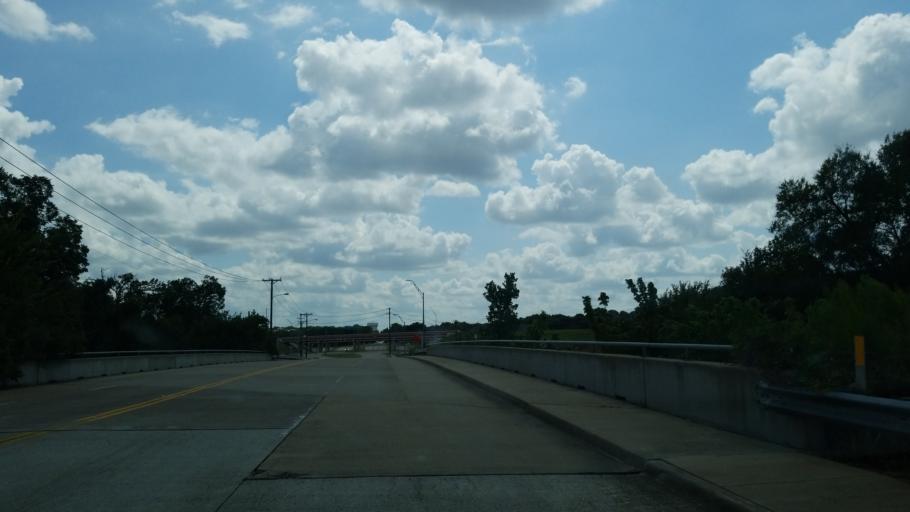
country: US
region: Texas
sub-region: Tarrant County
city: Grapevine
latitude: 32.8957
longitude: -97.0823
